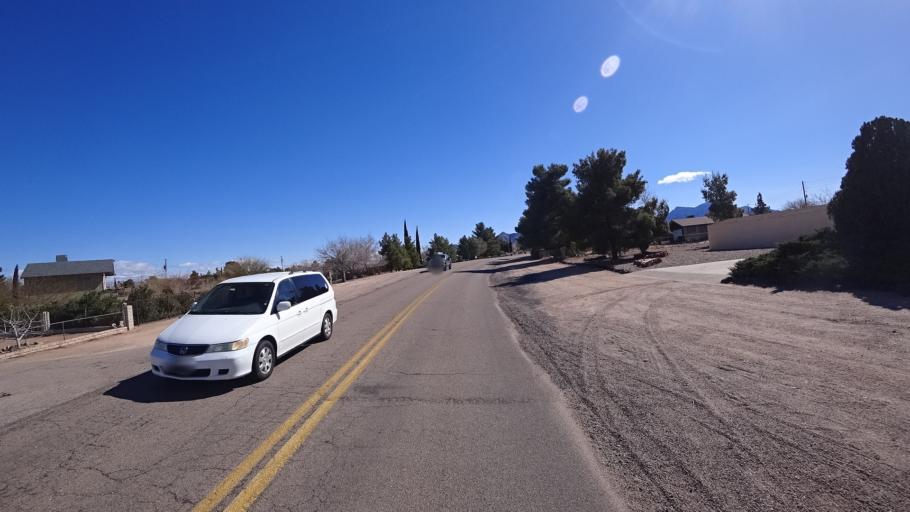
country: US
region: Arizona
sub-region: Mohave County
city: Kingman
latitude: 35.1992
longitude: -114.0102
